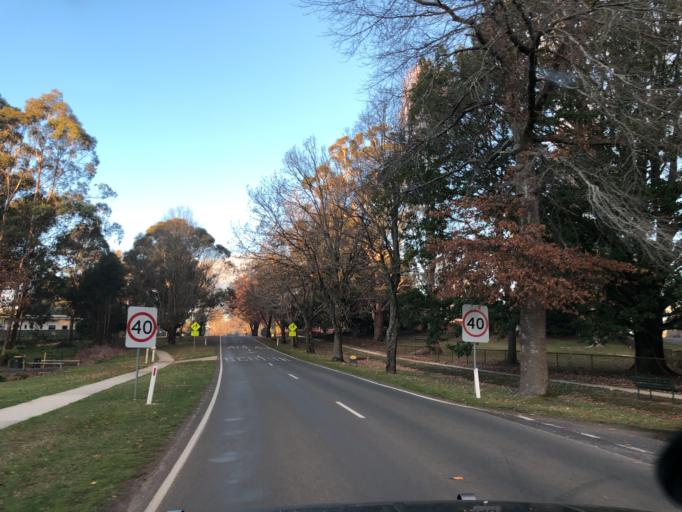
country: AU
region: Victoria
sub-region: Moorabool
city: Bacchus Marsh
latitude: -37.3892
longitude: 144.3261
